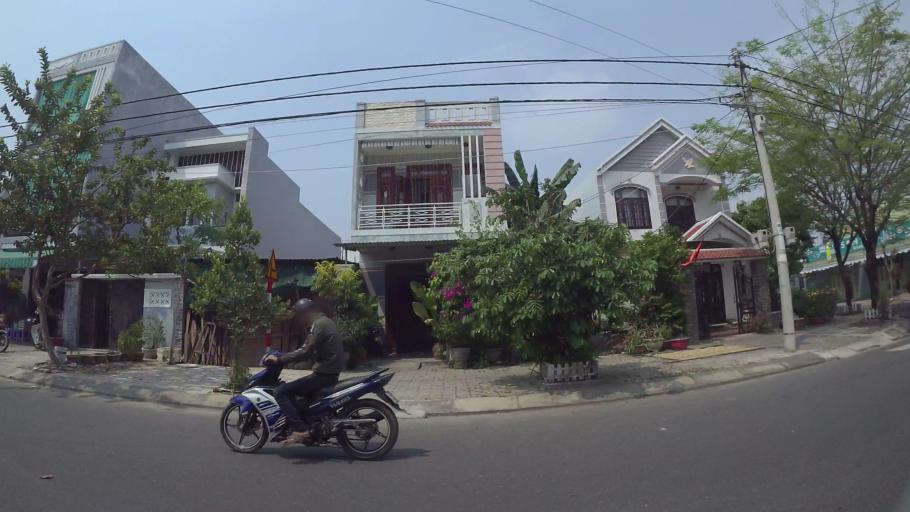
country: VN
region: Da Nang
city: Cam Le
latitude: 15.9866
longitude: 108.2138
